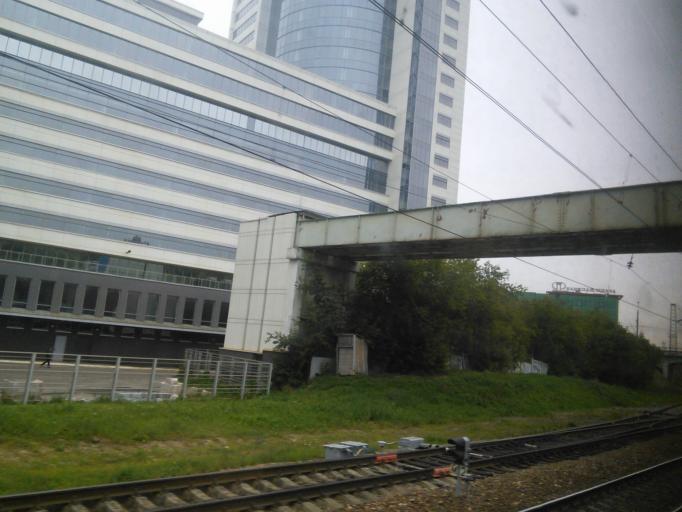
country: RU
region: Moskovskaya
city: Kastanayevo
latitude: 55.7372
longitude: 37.5064
